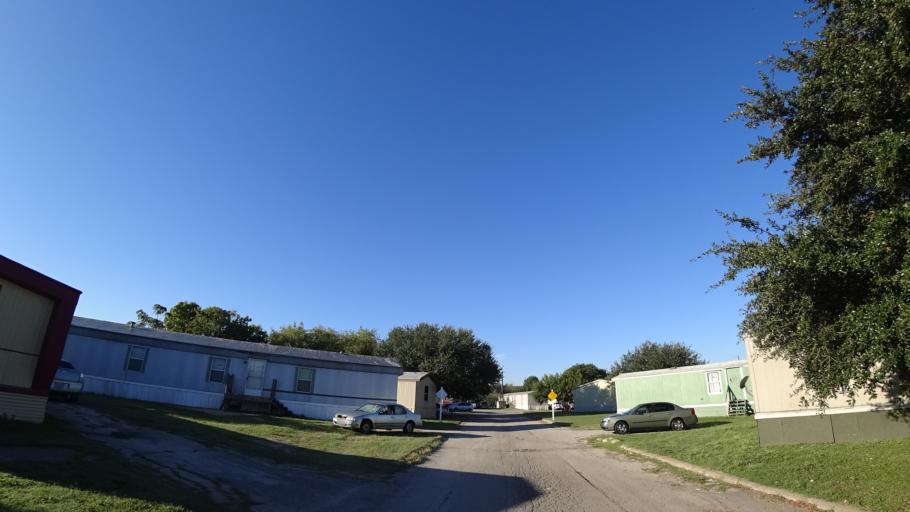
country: US
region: Texas
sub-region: Travis County
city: Austin
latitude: 30.2285
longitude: -97.6901
